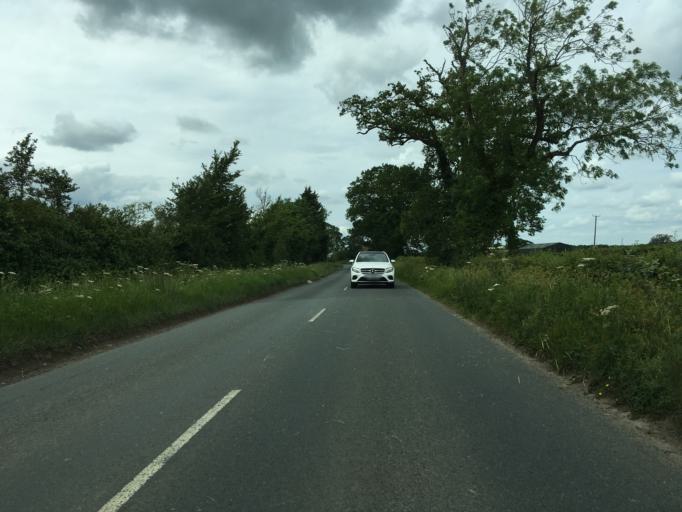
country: GB
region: England
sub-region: Wiltshire
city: Royal Wootton Bassett
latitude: 51.5610
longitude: -1.9294
